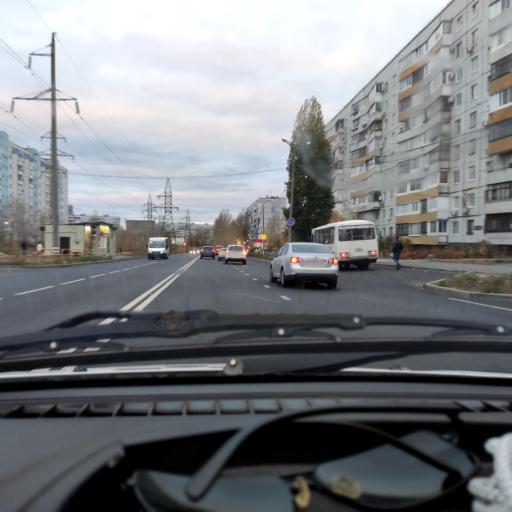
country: RU
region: Samara
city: Zhigulevsk
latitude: 53.4735
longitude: 49.5241
